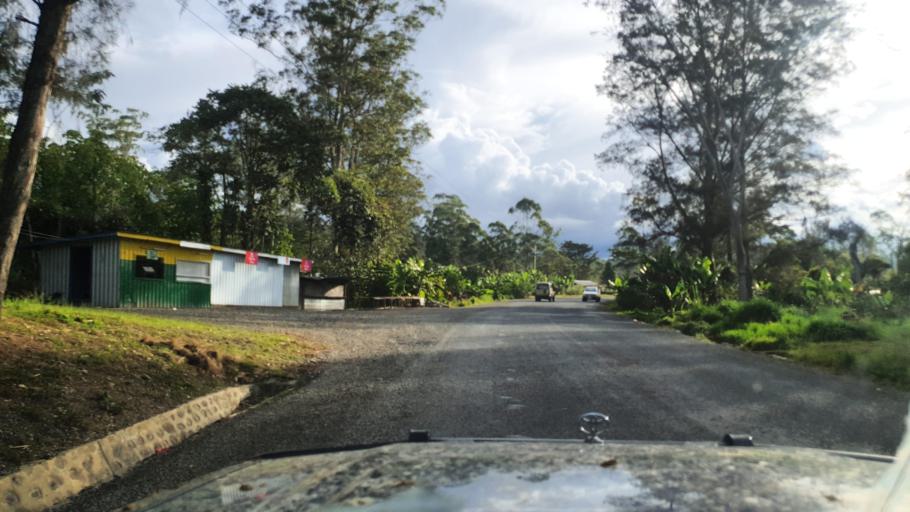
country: PG
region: Jiwaka
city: Minj
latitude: -5.8455
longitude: 144.5272
